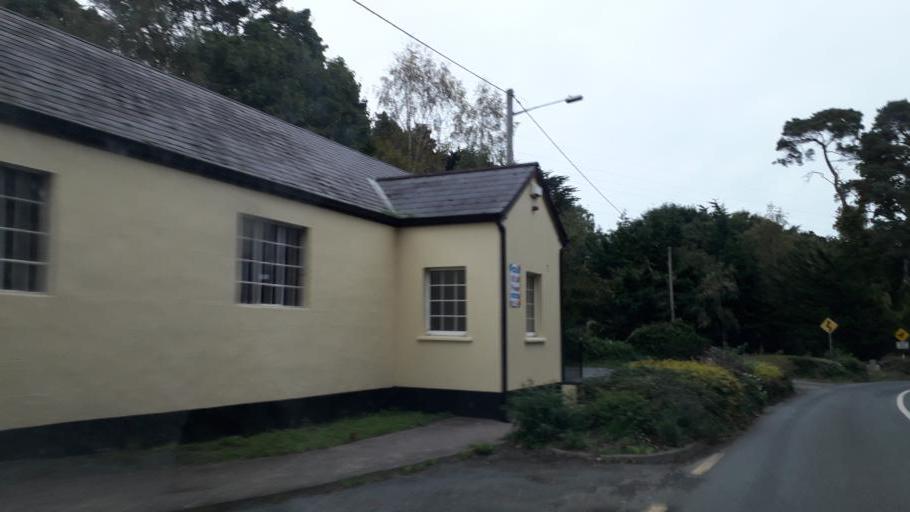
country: IE
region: Leinster
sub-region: Wicklow
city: Enniskerry
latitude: 53.1933
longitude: -6.1671
